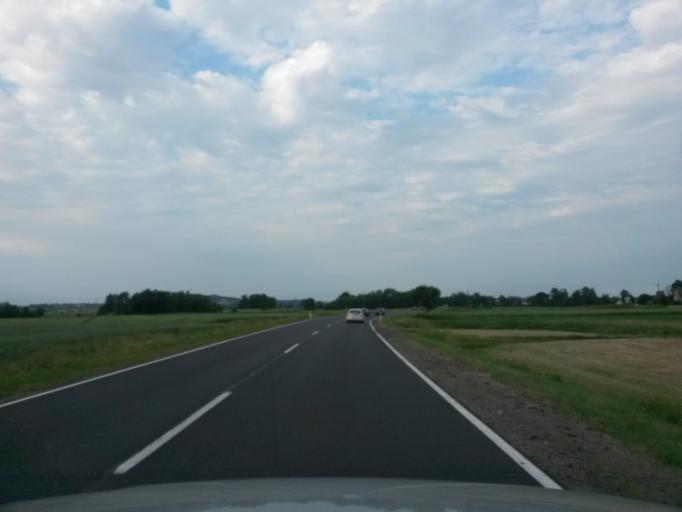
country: PL
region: Lower Silesian Voivodeship
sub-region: Powiat swidnicki
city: Strzegom
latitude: 50.9300
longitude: 16.3033
